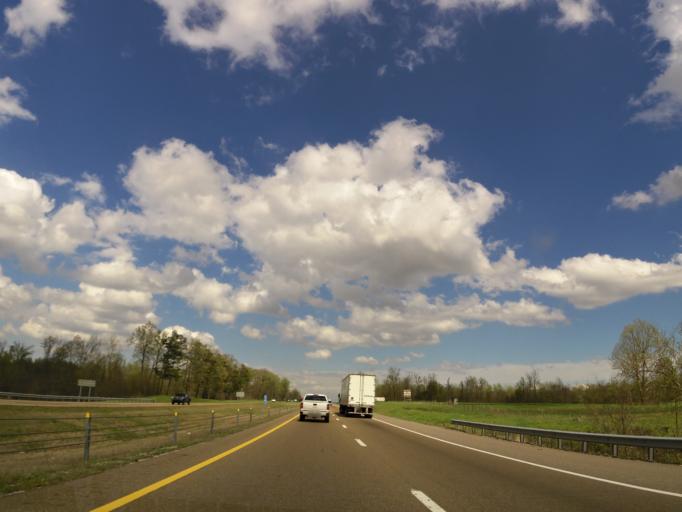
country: US
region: Tennessee
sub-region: Crockett County
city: Bells
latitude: 35.6286
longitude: -88.9636
